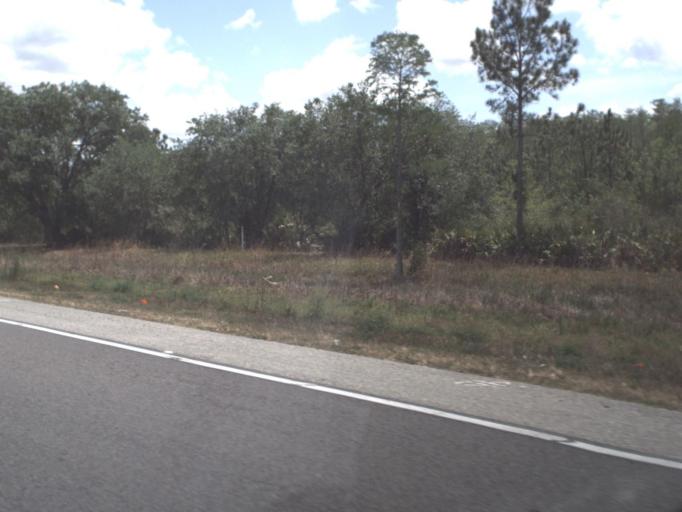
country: US
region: Florida
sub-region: Orange County
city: Wedgefield
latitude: 28.4515
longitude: -81.1528
